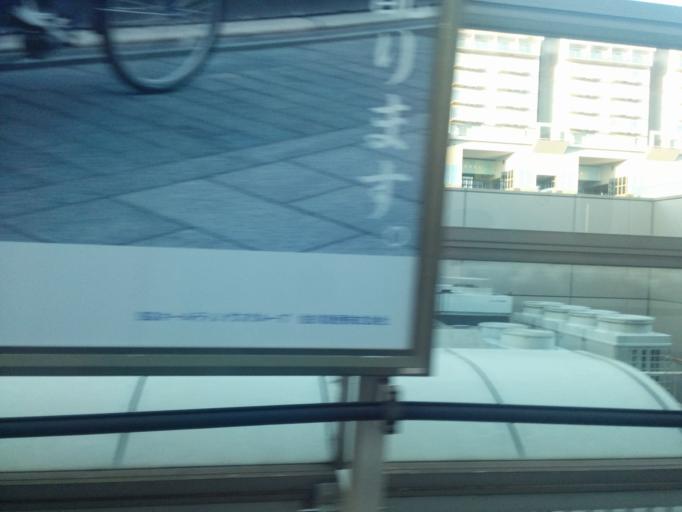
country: JP
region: Kyoto
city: Kyoto
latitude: 34.9848
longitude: 135.7583
